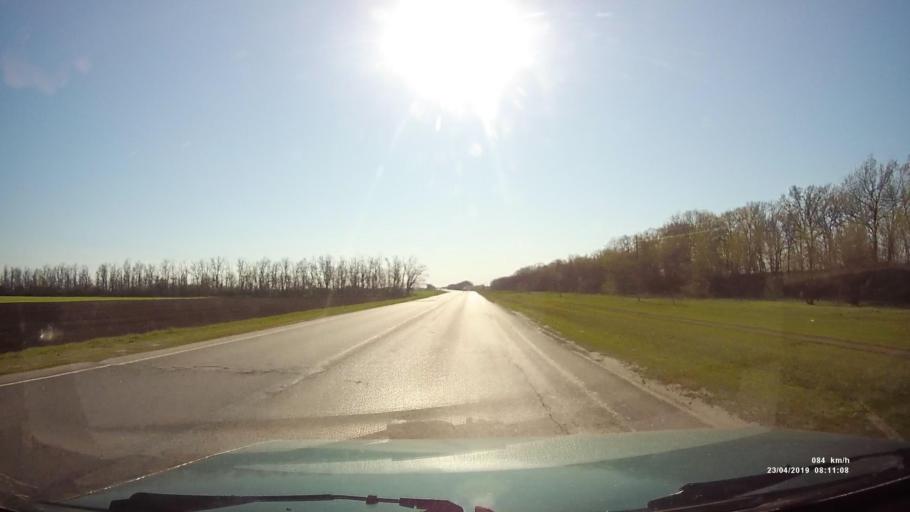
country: RU
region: Rostov
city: Yegorlykskaya
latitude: 46.5543
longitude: 40.6931
